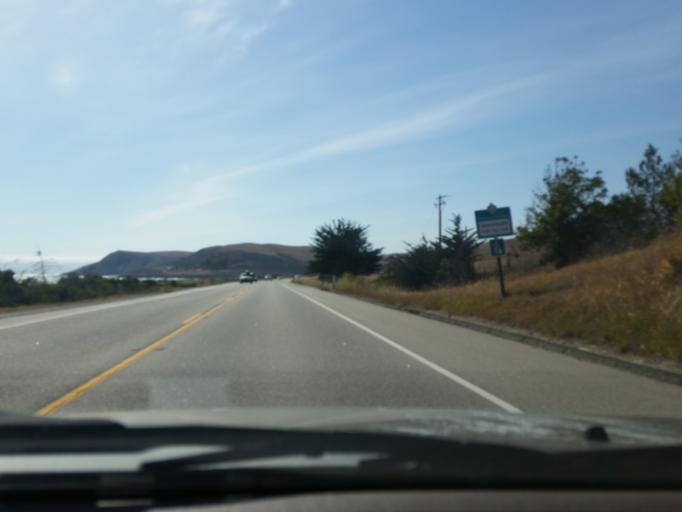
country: US
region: California
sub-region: San Luis Obispo County
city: Cayucos
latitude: 35.4545
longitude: -120.9527
